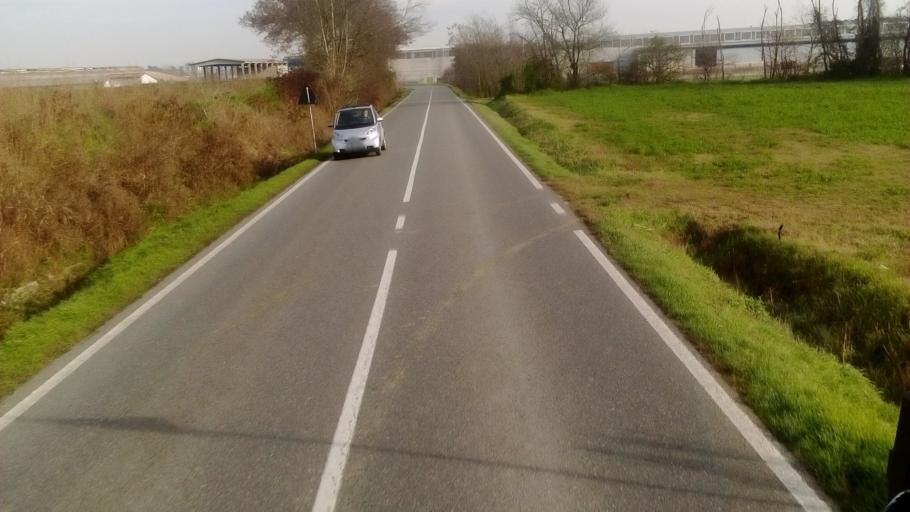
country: IT
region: Lombardy
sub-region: Provincia di Cremona
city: Castelleone
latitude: 45.2915
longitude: 9.7438
